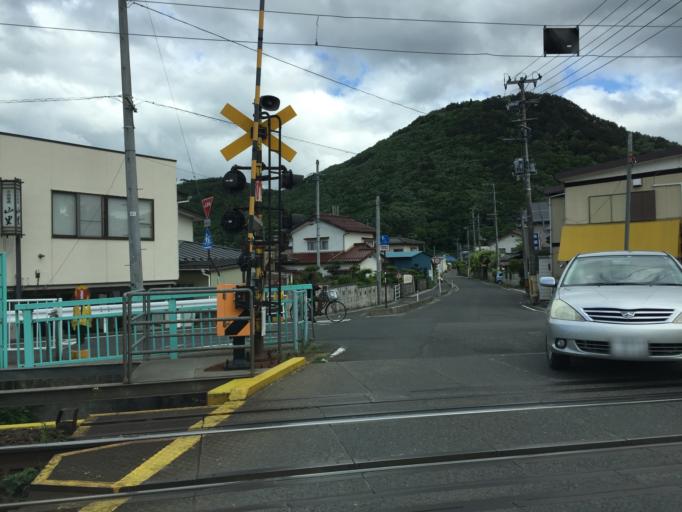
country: JP
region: Fukushima
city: Fukushima-shi
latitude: 37.7773
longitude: 140.4585
